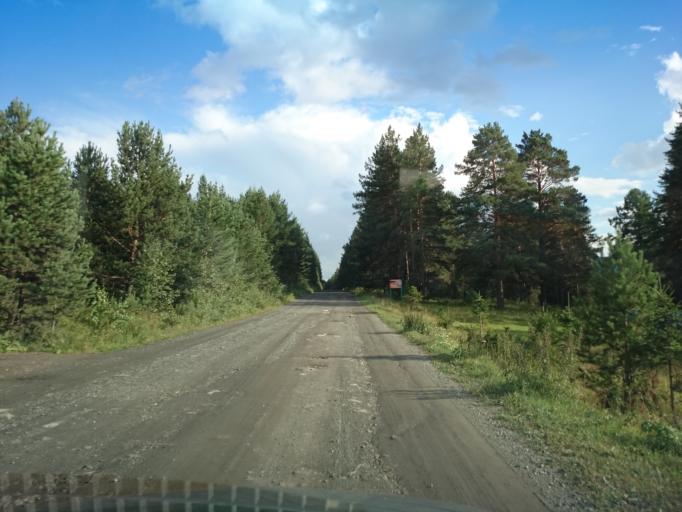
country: RU
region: Bashkortostan
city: Beloretsk
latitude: 54.0432
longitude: 58.3304
